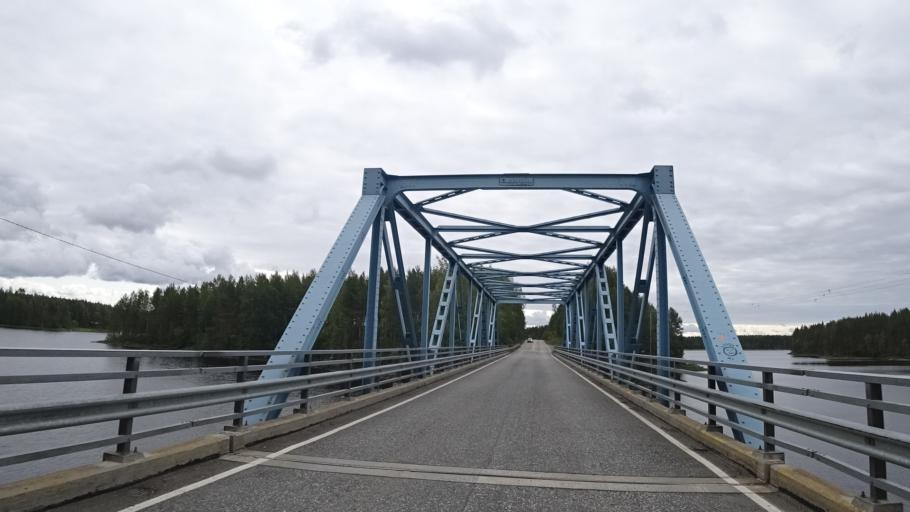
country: FI
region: North Karelia
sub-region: Joensuu
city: Ilomantsi
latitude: 62.6214
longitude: 31.1972
